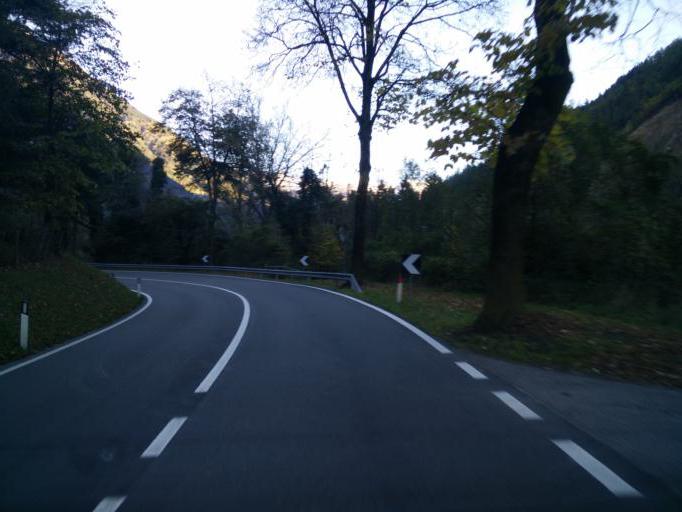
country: IT
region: Trentino-Alto Adige
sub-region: Bolzano
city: San Martino in Passiria
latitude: 46.7478
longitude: 11.2081
